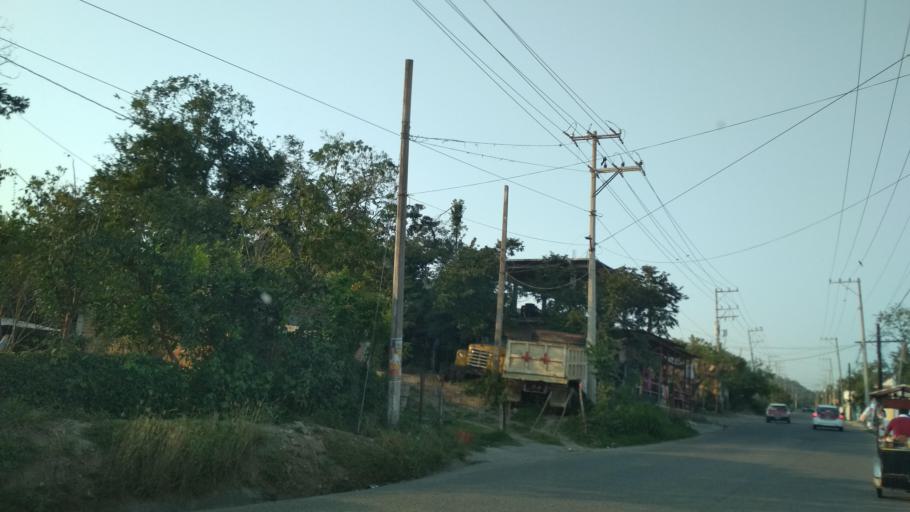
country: MM
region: Shan
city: Taunggyi
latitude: 20.4055
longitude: 97.3377
